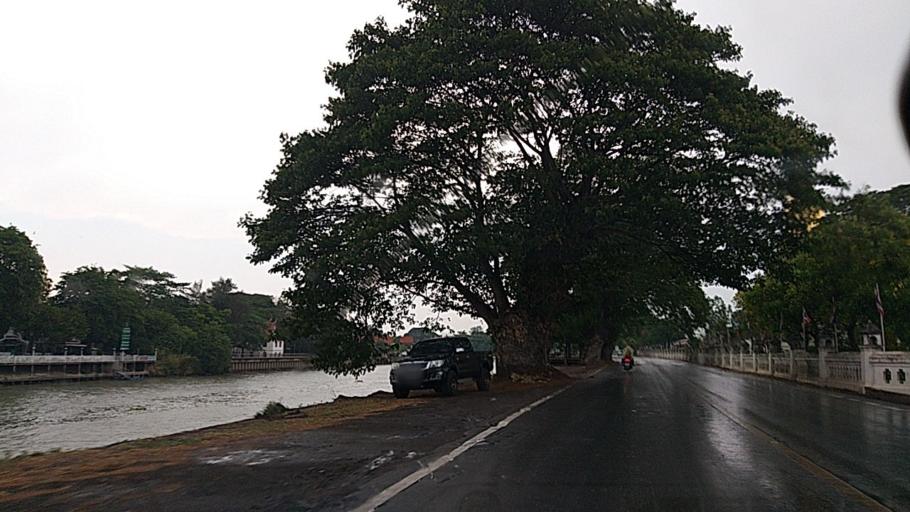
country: TH
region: Phra Nakhon Si Ayutthaya
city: Phra Nakhon Si Ayutthaya
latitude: 14.3518
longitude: 100.5467
